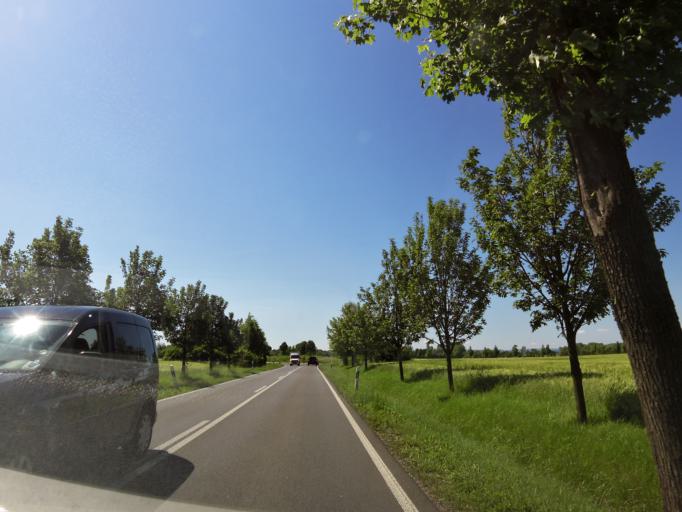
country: DE
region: Thuringia
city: Gotha
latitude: 50.9251
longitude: 10.7003
